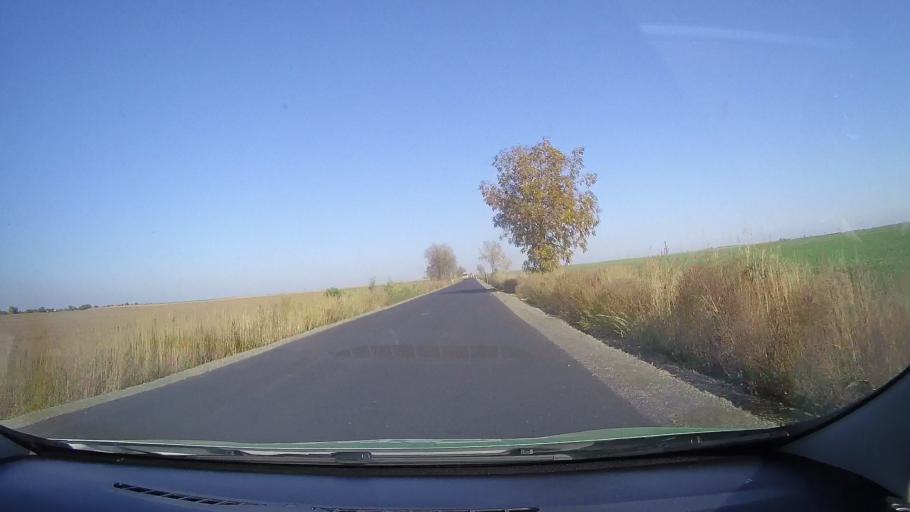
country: RO
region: Satu Mare
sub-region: Comuna Tiream
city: Tiream
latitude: 47.6264
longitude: 22.4678
